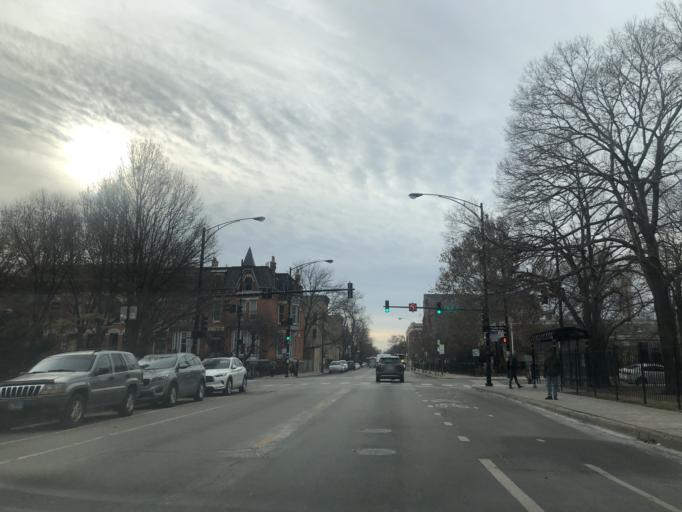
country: US
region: Illinois
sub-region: Cook County
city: Chicago
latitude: 41.9076
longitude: -87.6774
